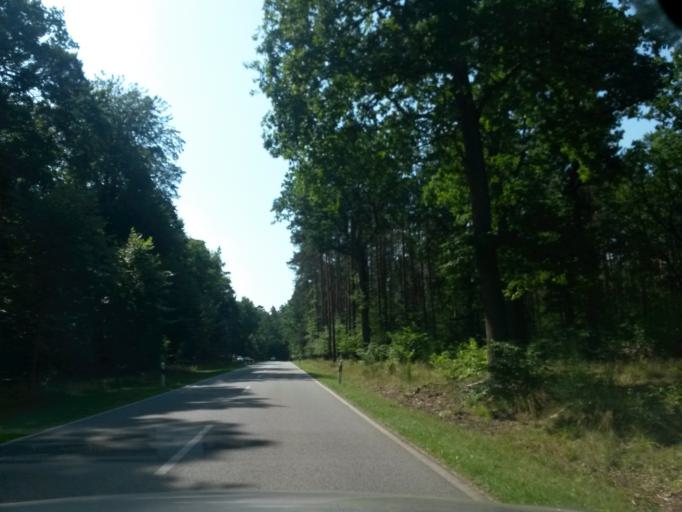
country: DE
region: Brandenburg
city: Marienwerder
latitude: 52.9022
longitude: 13.6447
